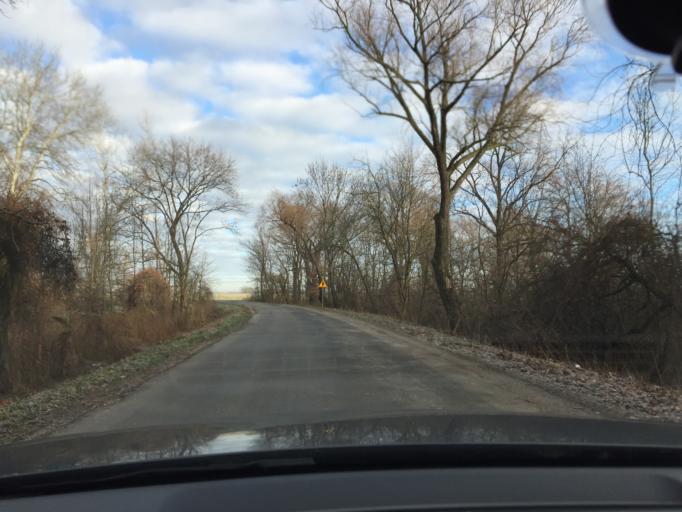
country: PL
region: Lower Silesian Voivodeship
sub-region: Powiat sredzki
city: Udanin
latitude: 51.0462
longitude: 16.5175
